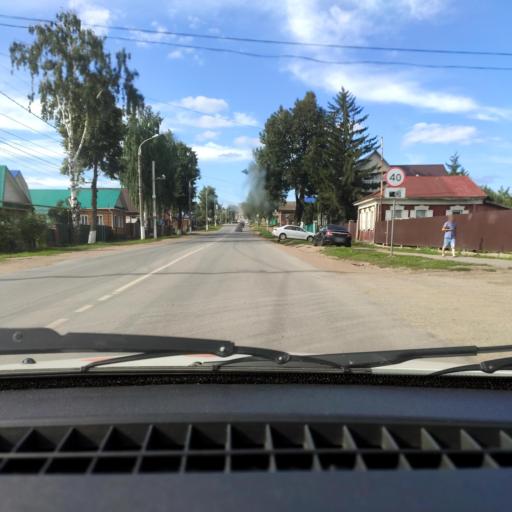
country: RU
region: Bashkortostan
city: Blagoveshchensk
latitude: 55.0379
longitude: 55.9635
